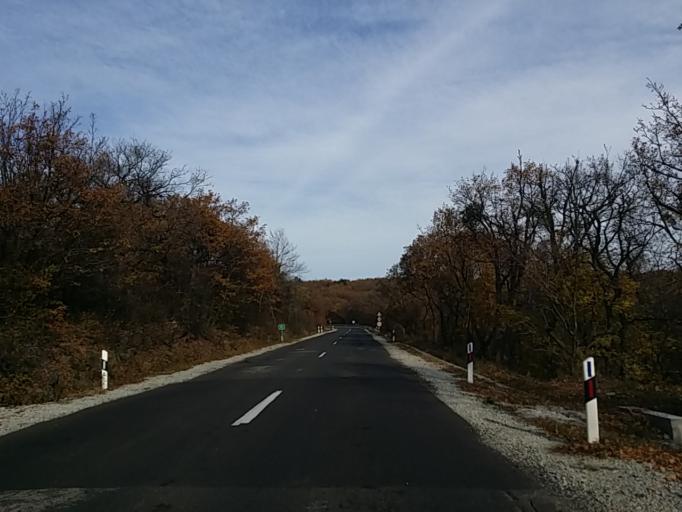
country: HU
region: Heves
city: Gyongyossolymos
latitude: 47.8419
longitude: 19.9610
